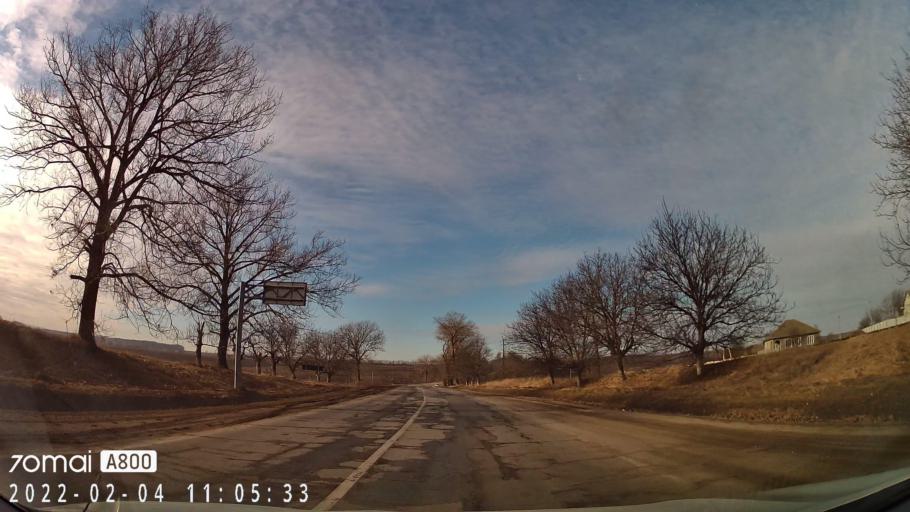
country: RO
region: Botosani
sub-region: Comuna Radauti-Prut
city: Miorcani
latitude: 48.2886
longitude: 26.8699
